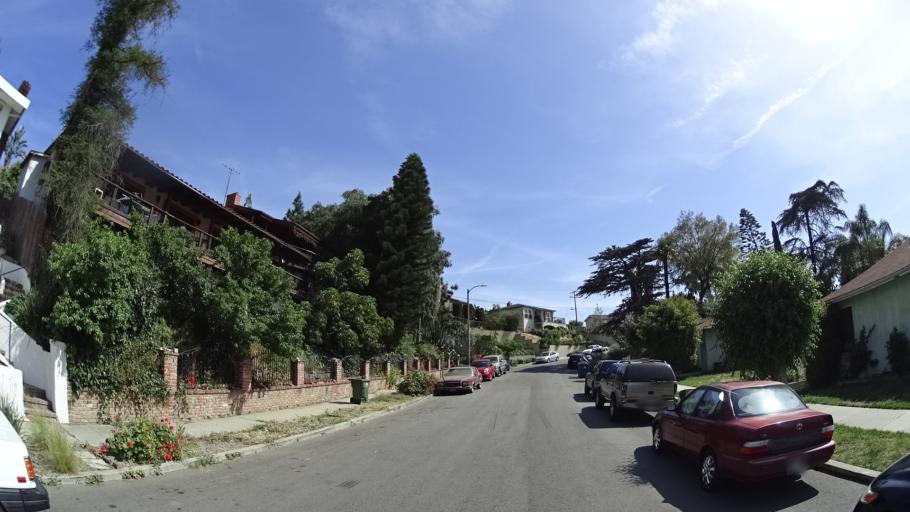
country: US
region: California
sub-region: Los Angeles County
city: Belvedere
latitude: 34.0654
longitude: -118.1845
